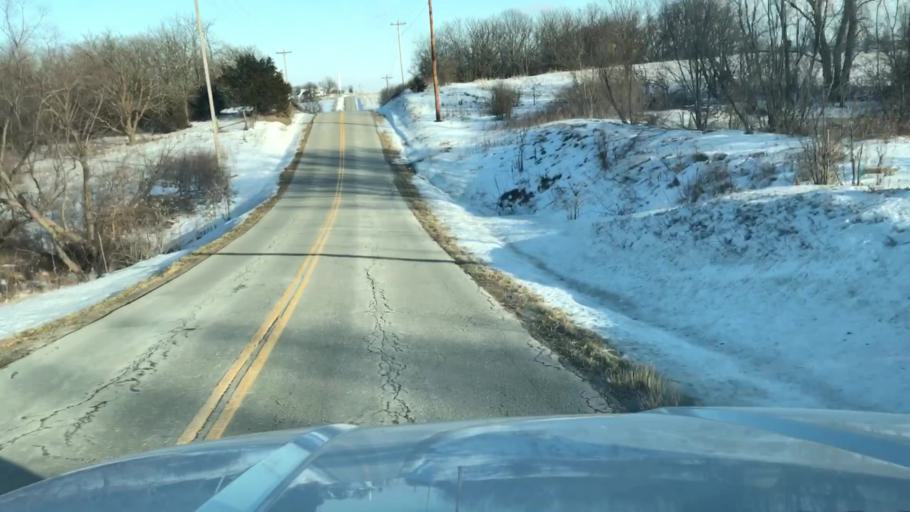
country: US
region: Missouri
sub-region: Andrew County
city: Savannah
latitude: 40.0246
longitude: -94.8952
